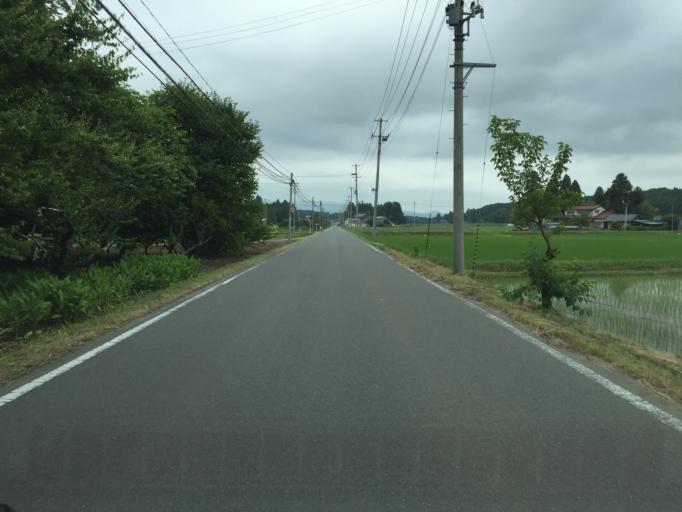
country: JP
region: Fukushima
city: Namie
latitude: 37.7273
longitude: 140.9351
